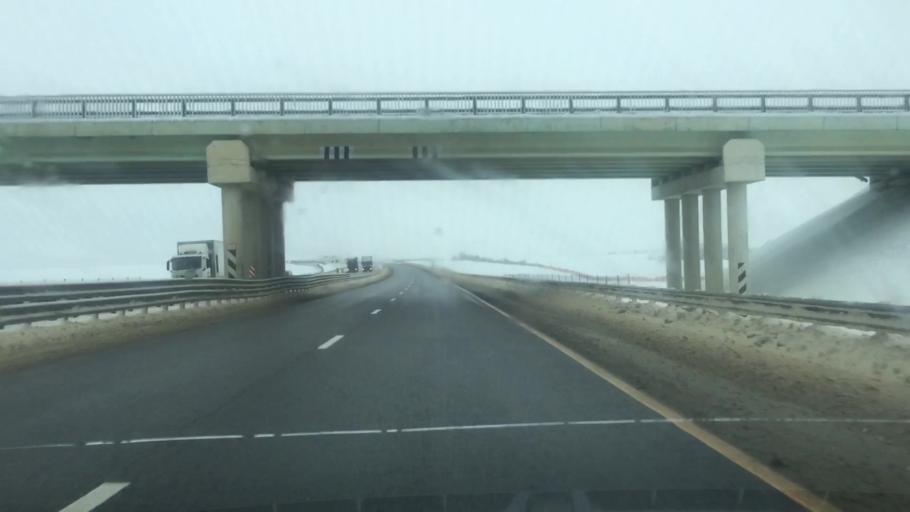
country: RU
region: Tula
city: Yefremov
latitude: 53.2251
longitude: 38.2086
